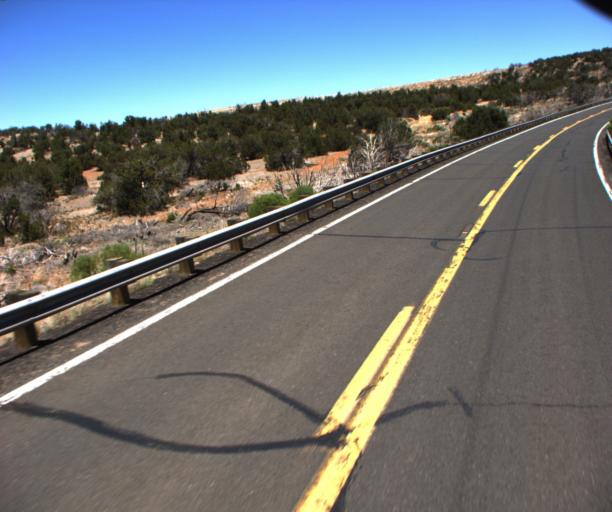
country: US
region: Arizona
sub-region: Coconino County
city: LeChee
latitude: 34.7288
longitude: -111.0800
